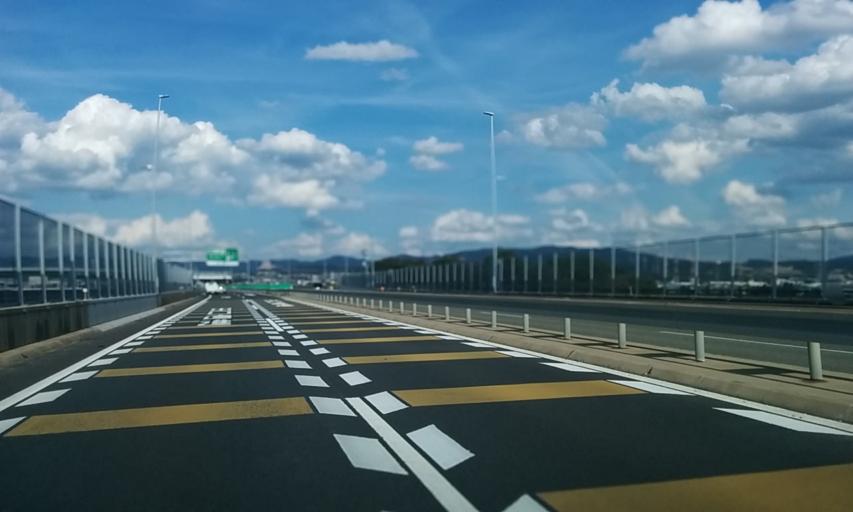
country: JP
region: Kyoto
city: Tanabe
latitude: 34.8425
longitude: 135.7586
